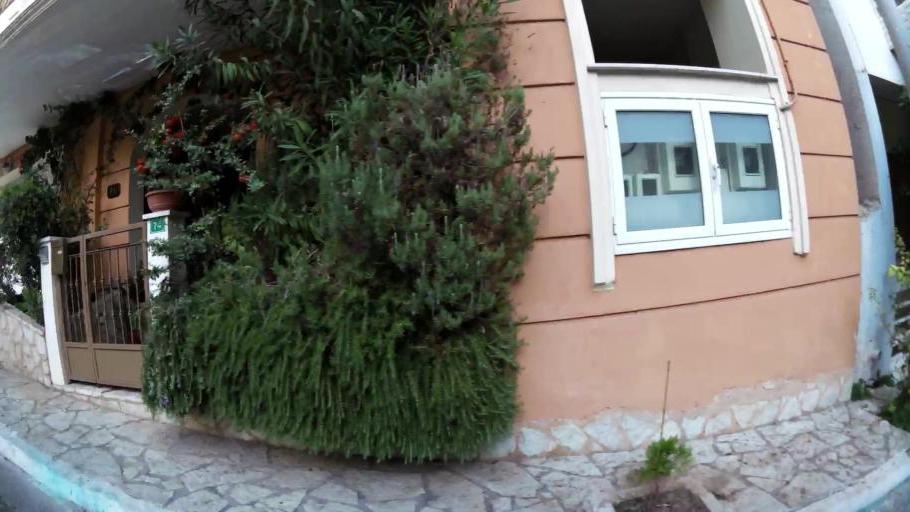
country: GR
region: Attica
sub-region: Nomarchia Athinas
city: Petroupolis
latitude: 38.0460
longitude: 23.6905
